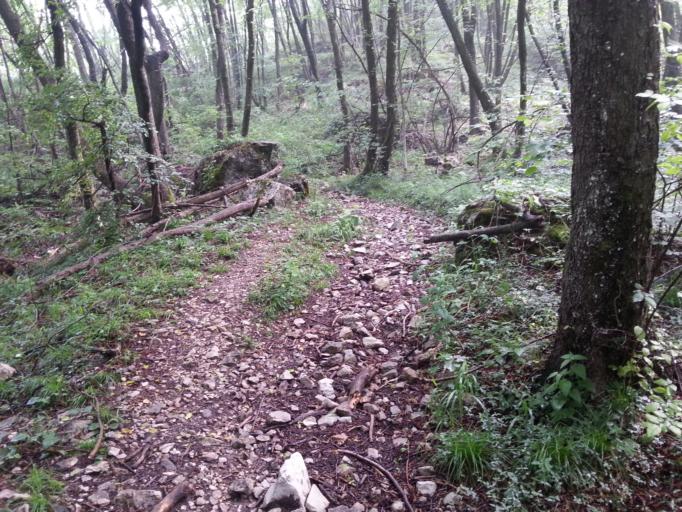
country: IT
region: Lombardy
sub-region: Provincia di Varese
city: Viggiu
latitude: 45.8859
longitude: 8.9075
